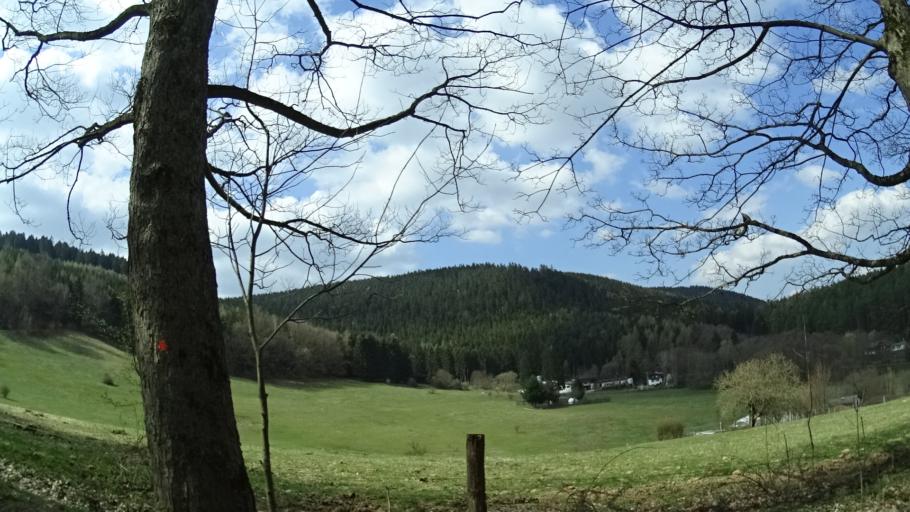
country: DE
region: Thuringia
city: Frankenhain
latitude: 50.7540
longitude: 10.7813
